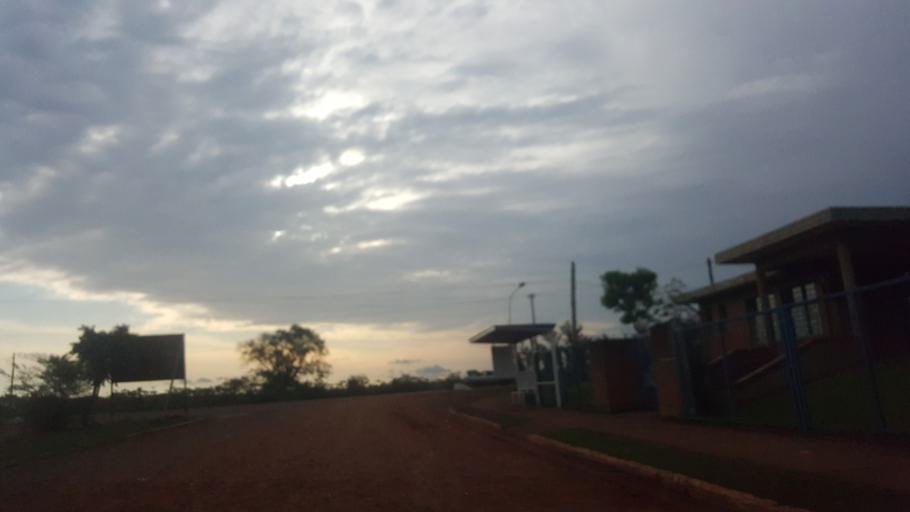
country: AR
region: Misiones
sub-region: Departamento de Candelaria
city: Candelaria
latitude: -27.4764
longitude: -55.7459
